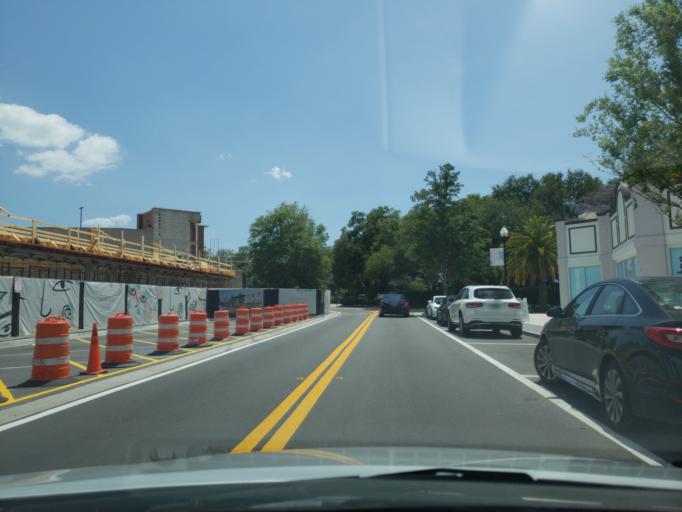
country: US
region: Florida
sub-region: Hillsborough County
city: Tampa
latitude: 27.9358
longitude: -82.4764
